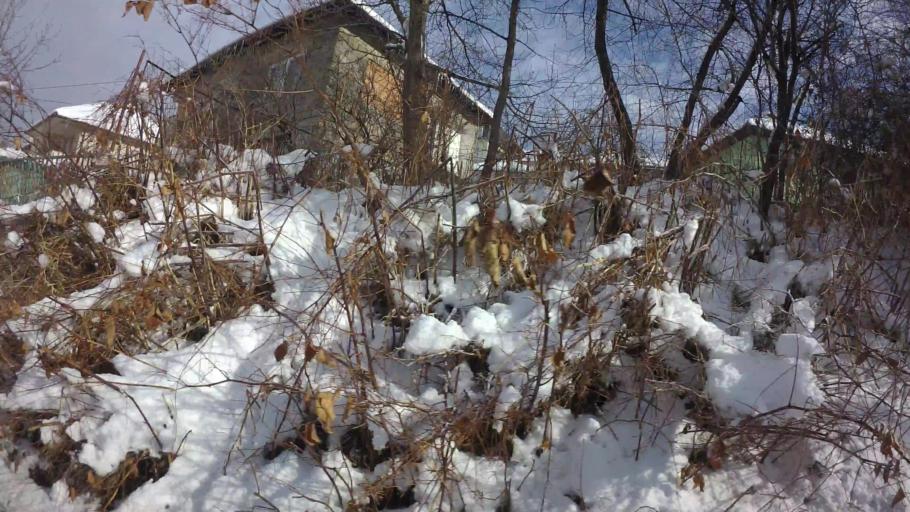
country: BA
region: Federation of Bosnia and Herzegovina
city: Kobilja Glava
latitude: 43.8735
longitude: 18.4193
